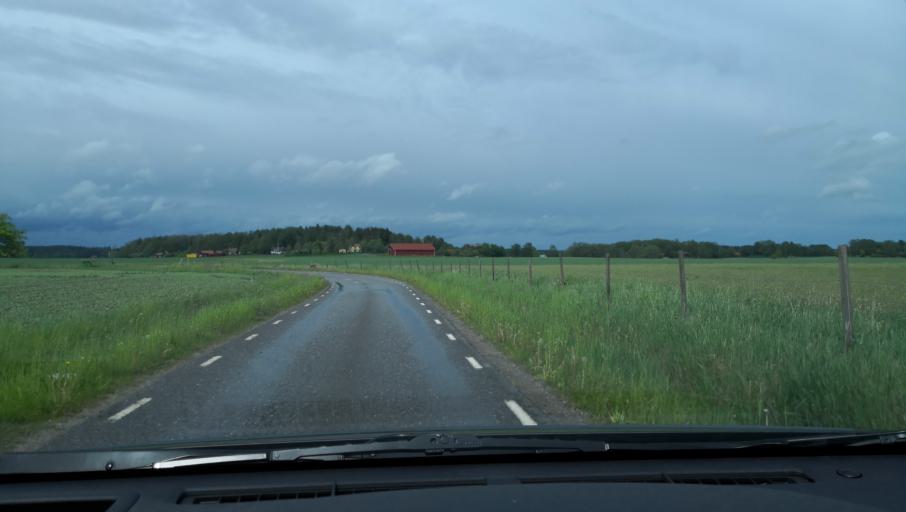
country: SE
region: Uppsala
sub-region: Enkopings Kommun
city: Orsundsbro
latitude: 59.7144
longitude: 17.4238
